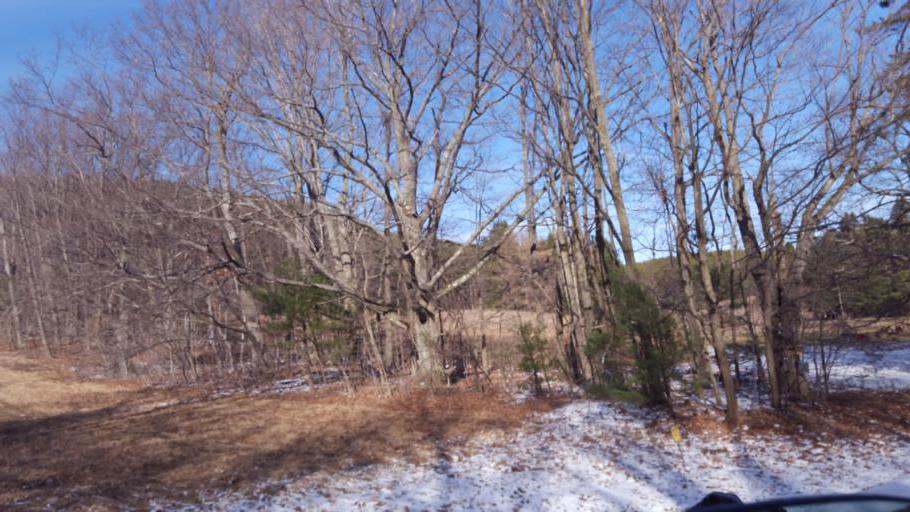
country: US
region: New York
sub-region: Allegany County
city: Wellsville
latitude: 42.0841
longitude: -77.9803
